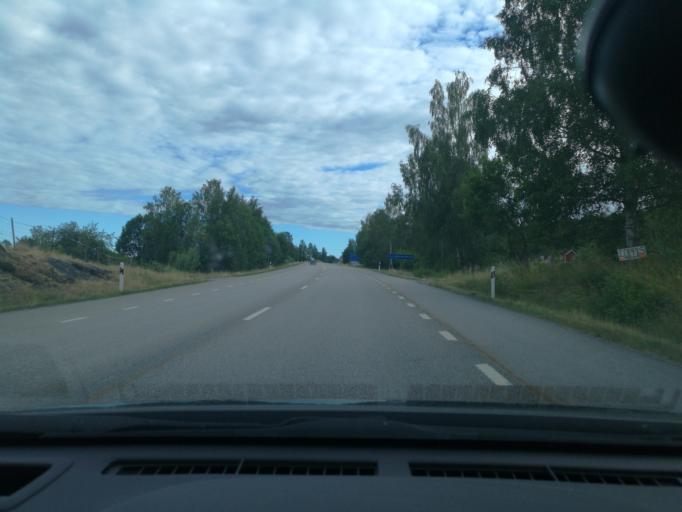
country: SE
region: Kalmar
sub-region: Vasterviks Kommun
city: Ankarsrum
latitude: 57.7172
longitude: 16.4503
